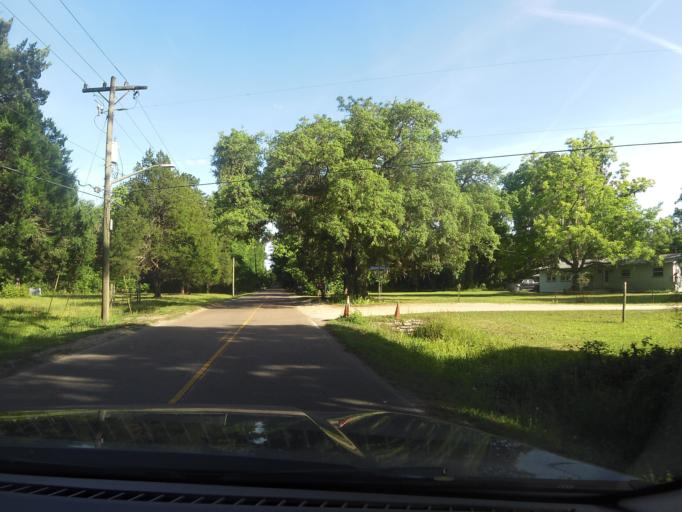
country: US
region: Florida
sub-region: Nassau County
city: Nassau Village-Ratliff
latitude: 30.4630
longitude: -81.8336
